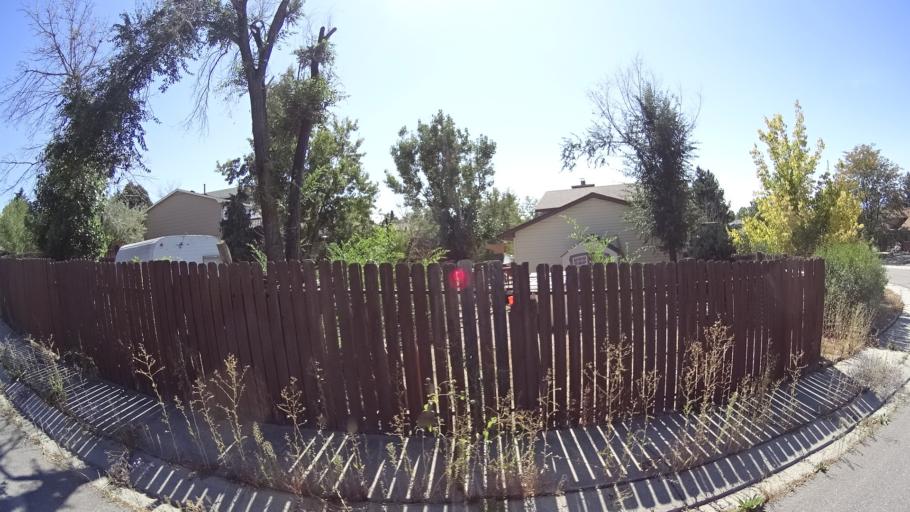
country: US
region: Colorado
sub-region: El Paso County
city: Cimarron Hills
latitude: 38.9159
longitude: -104.7670
